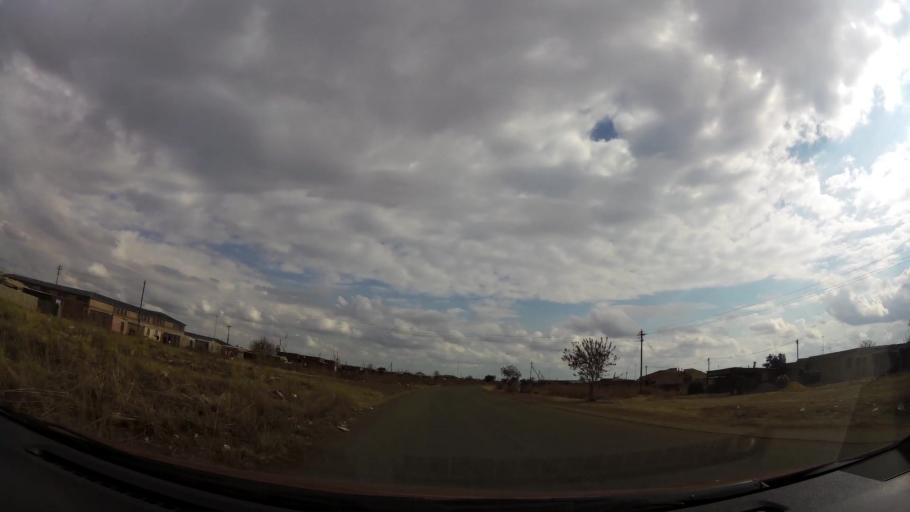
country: ZA
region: Gauteng
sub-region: Sedibeng District Municipality
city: Vanderbijlpark
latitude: -26.6812
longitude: 27.7866
